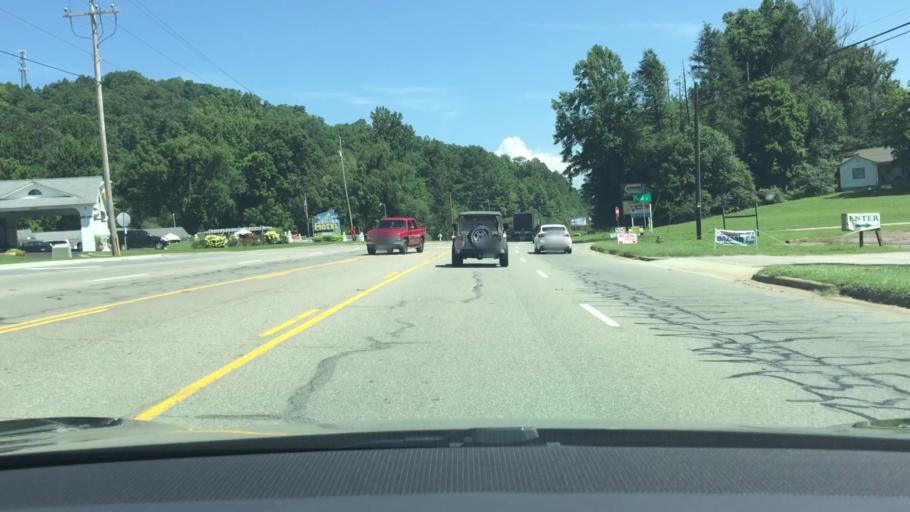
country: US
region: North Carolina
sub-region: Macon County
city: Franklin
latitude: 35.1384
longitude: -83.3983
